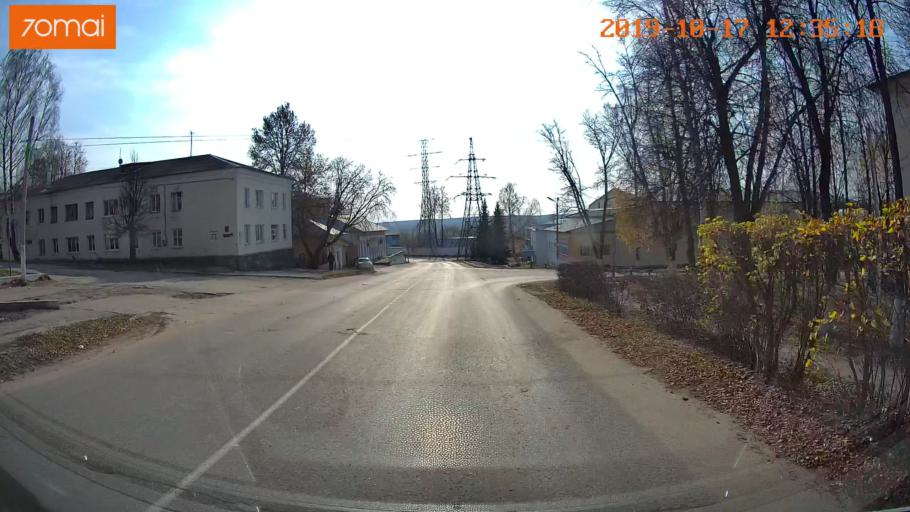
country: RU
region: Rjazan
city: Kasimov
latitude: 54.9444
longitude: 41.3700
